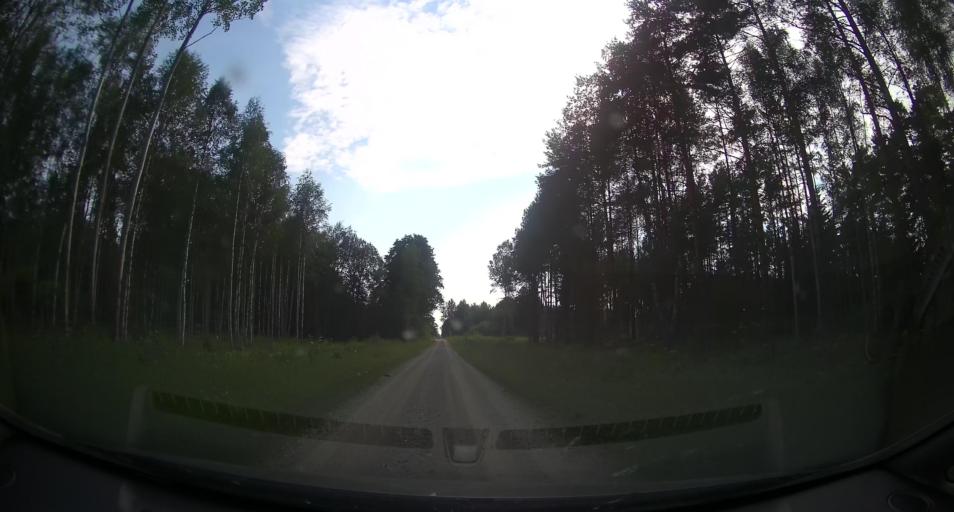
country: EE
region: Laeaene
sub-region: Lihula vald
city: Lihula
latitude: 58.6477
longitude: 23.7847
